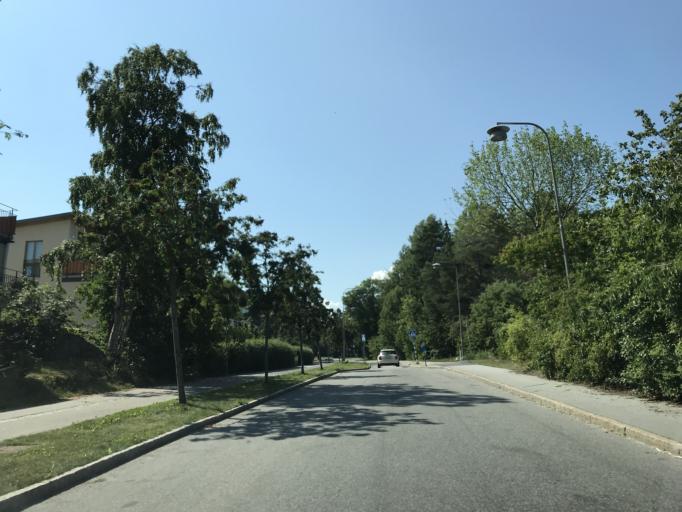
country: SE
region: Stockholm
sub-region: Stockholms Kommun
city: Bromma
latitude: 59.3302
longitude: 17.9568
